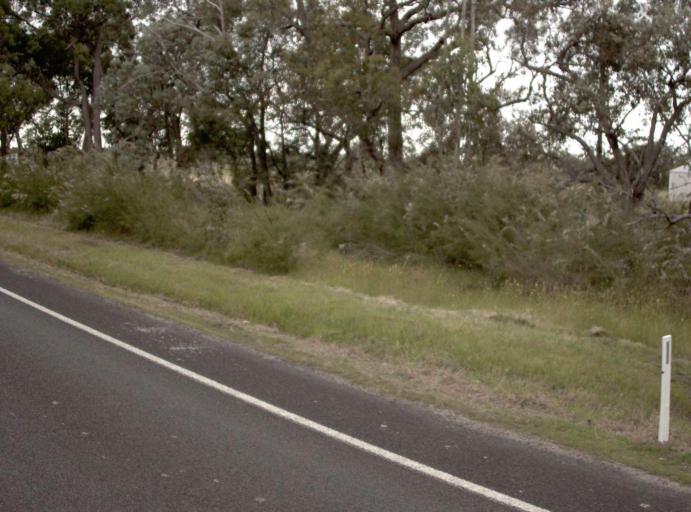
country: AU
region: Victoria
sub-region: Wellington
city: Sale
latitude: -38.3467
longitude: 147.0011
